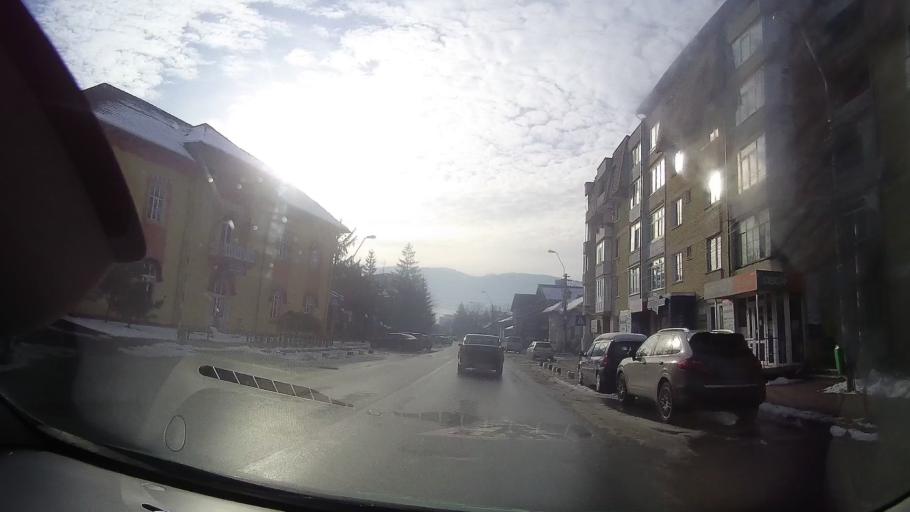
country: RO
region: Neamt
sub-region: Municipiul Piatra-Neamt
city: Valeni
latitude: 46.9353
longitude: 26.3745
